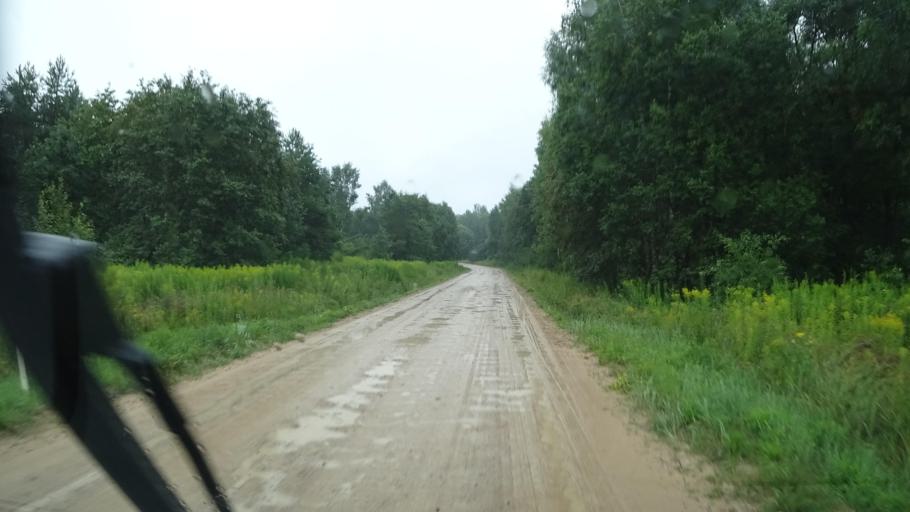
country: LV
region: Lecava
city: Iecava
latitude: 56.6627
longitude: 24.1688
